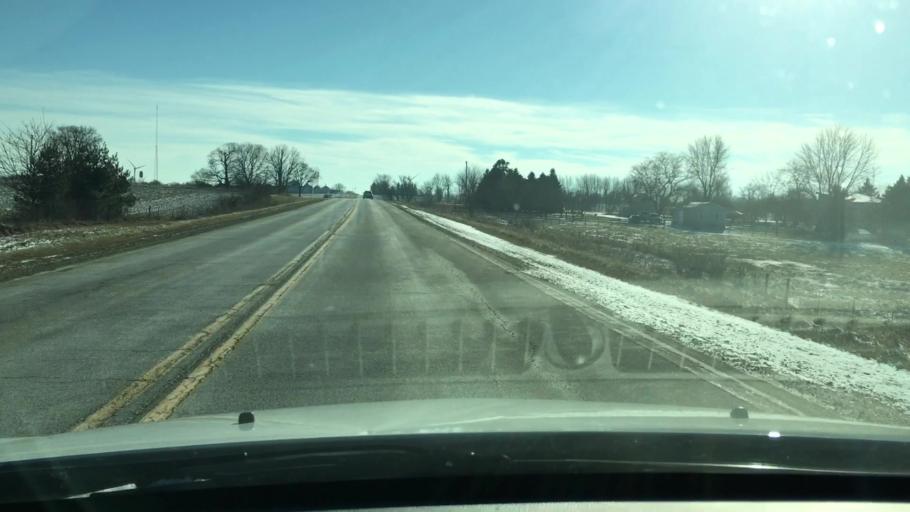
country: US
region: Illinois
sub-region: LaSalle County
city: Mendota
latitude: 41.7089
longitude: -89.0915
